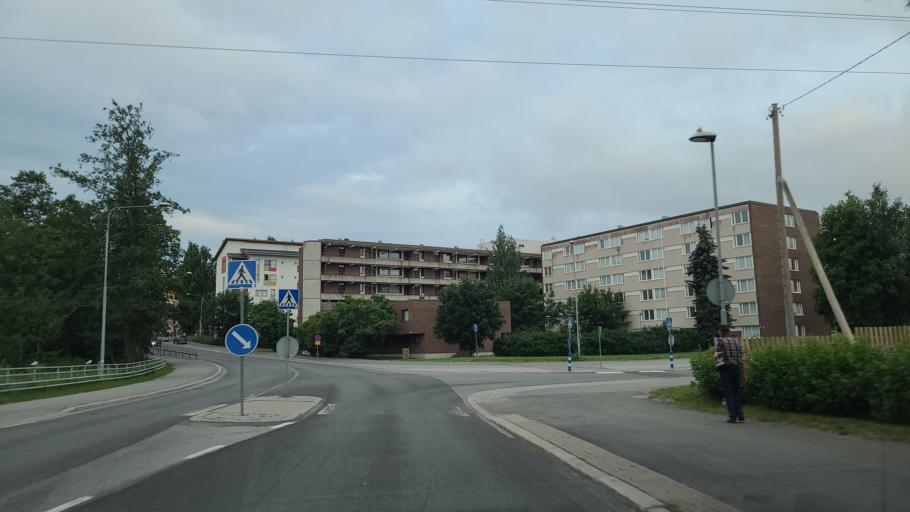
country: FI
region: Ostrobothnia
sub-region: Vaasa
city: Vaasa
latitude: 63.1054
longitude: 21.6175
